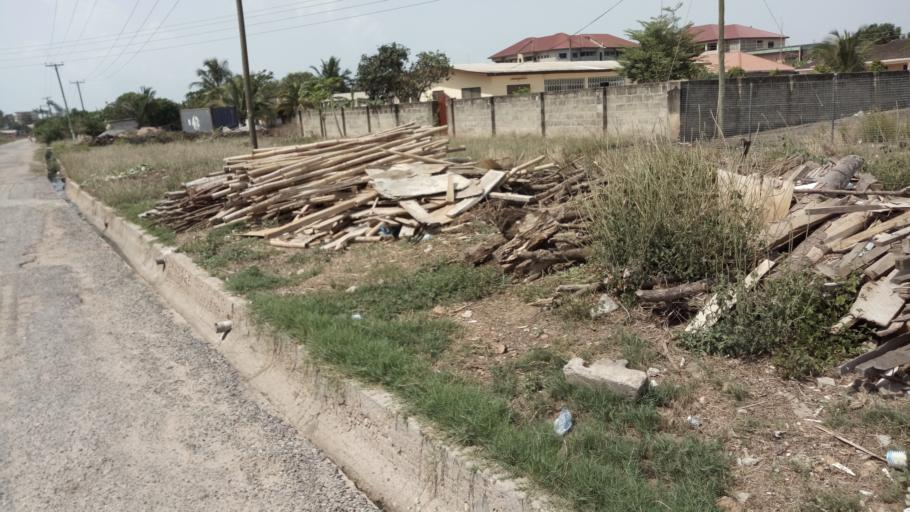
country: GH
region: Central
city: Winneba
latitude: 5.3604
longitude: -0.6357
